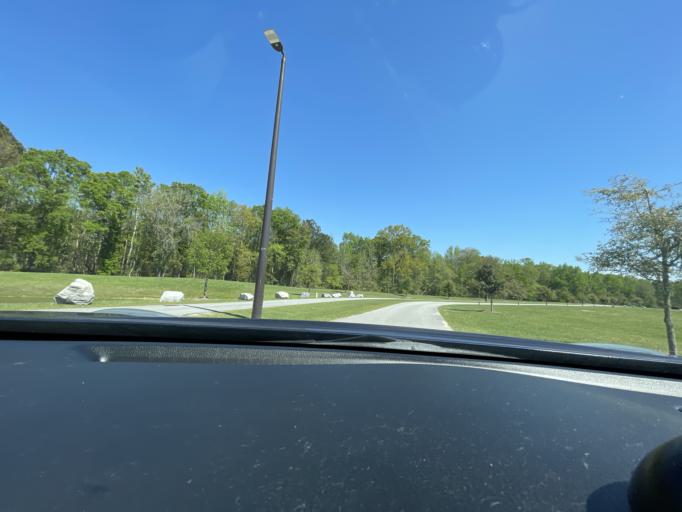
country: US
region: Georgia
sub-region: Chatham County
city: Pooler
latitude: 32.1360
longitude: -81.2641
